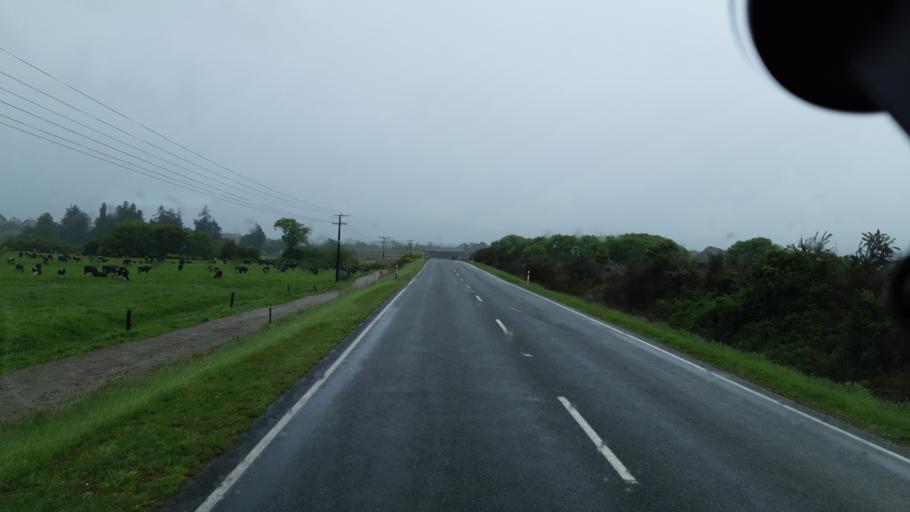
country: NZ
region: West Coast
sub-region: Buller District
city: Westport
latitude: -42.1519
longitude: 171.7602
